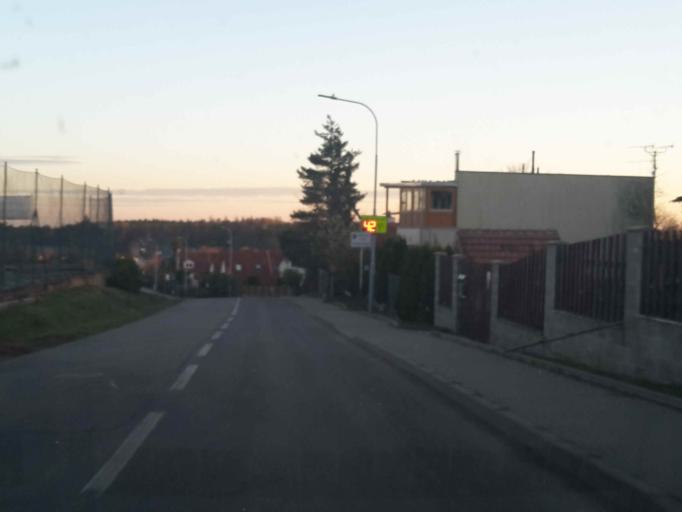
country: CZ
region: South Moravian
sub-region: Okres Blansko
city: Adamov
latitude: 49.2909
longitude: 16.6300
